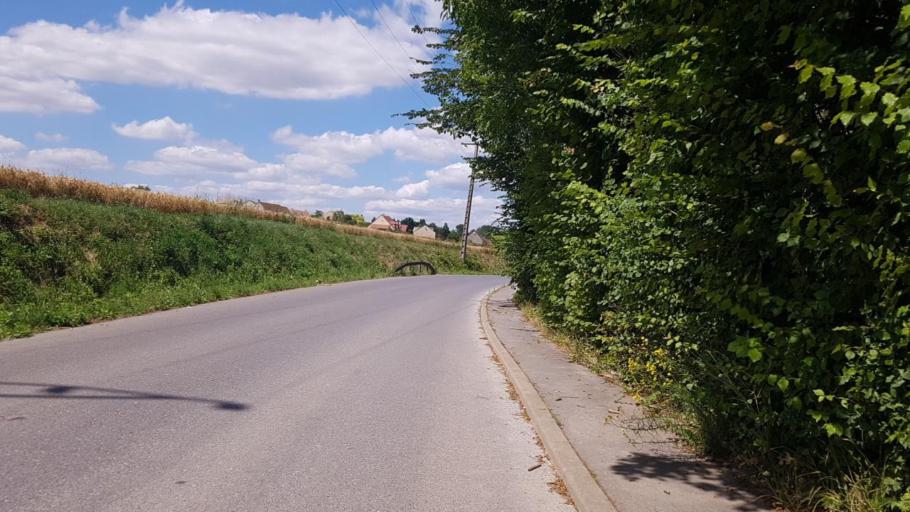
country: FR
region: Ile-de-France
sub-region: Departement de Seine-et-Marne
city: Juilly
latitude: 48.9871
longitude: 2.6694
